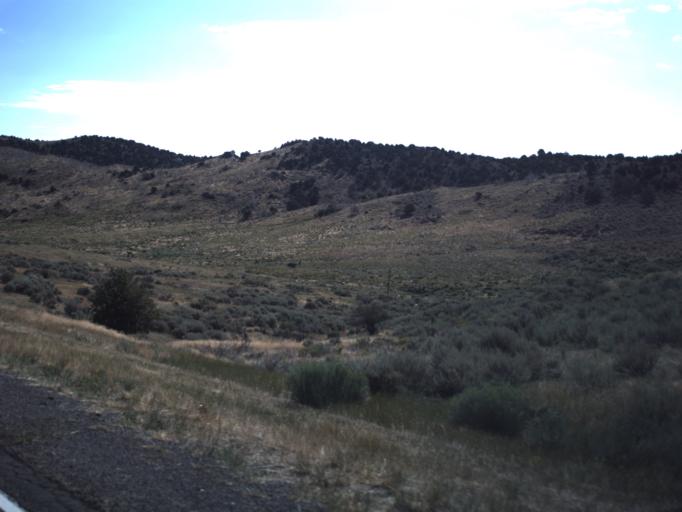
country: US
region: Utah
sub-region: Utah County
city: Genola
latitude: 39.9645
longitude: -112.0952
